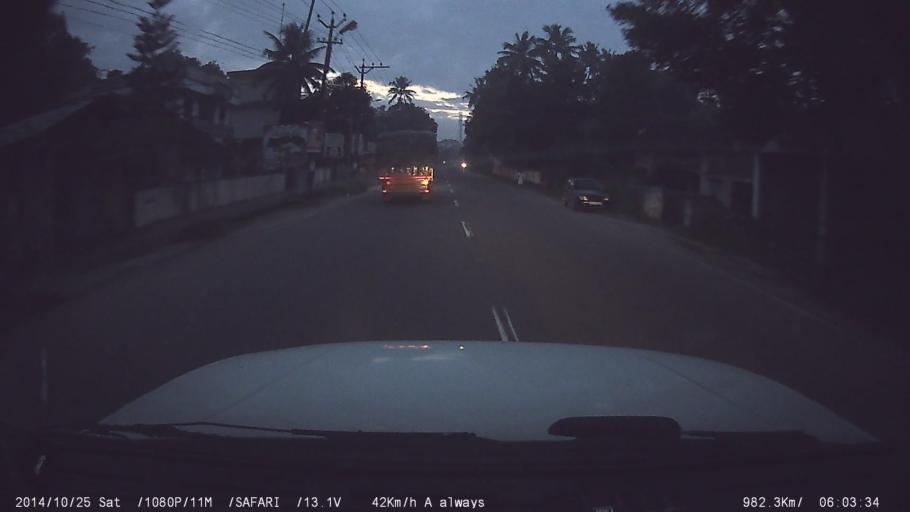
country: IN
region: Kerala
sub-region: Ernakulam
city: Angamali
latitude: 10.1880
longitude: 76.3940
